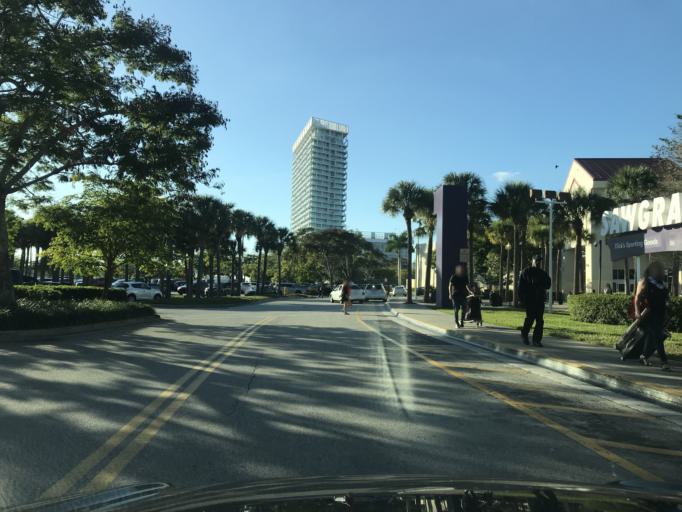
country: US
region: Florida
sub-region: Broward County
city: Pine Island Ridge
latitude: 26.1487
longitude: -80.3249
